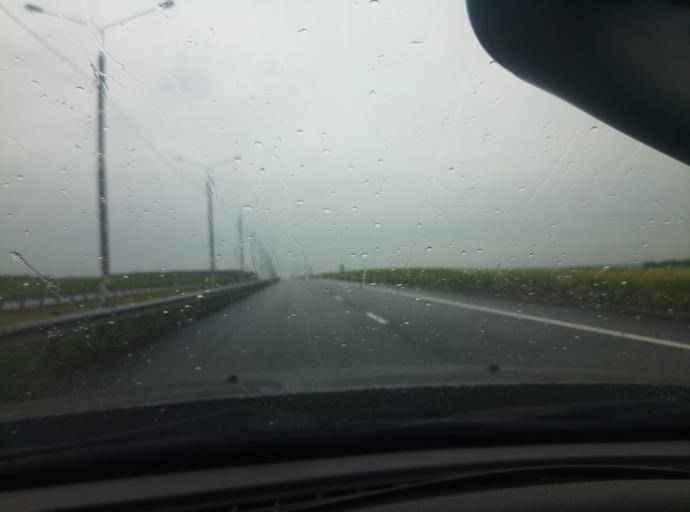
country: RU
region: Tula
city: Zaokskiy
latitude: 54.7056
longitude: 37.5134
